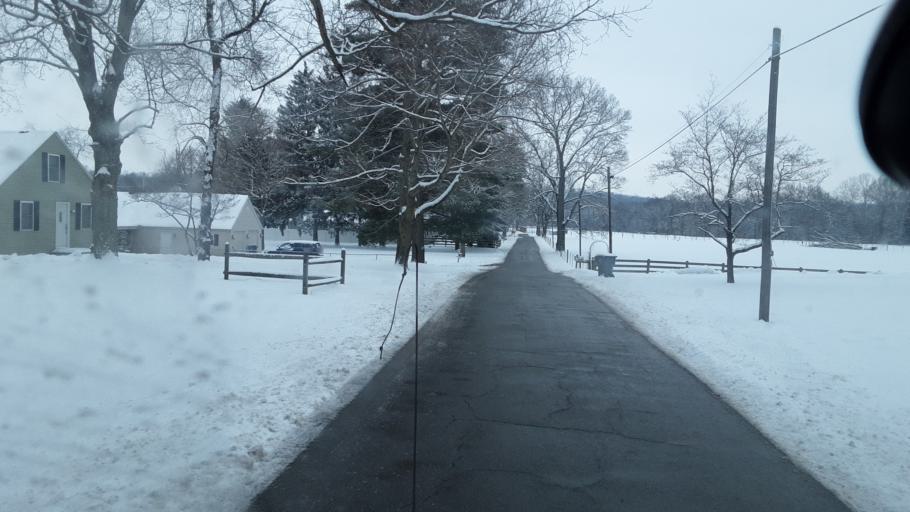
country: US
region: Ohio
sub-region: Licking County
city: Granville
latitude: 40.0641
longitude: -82.5003
